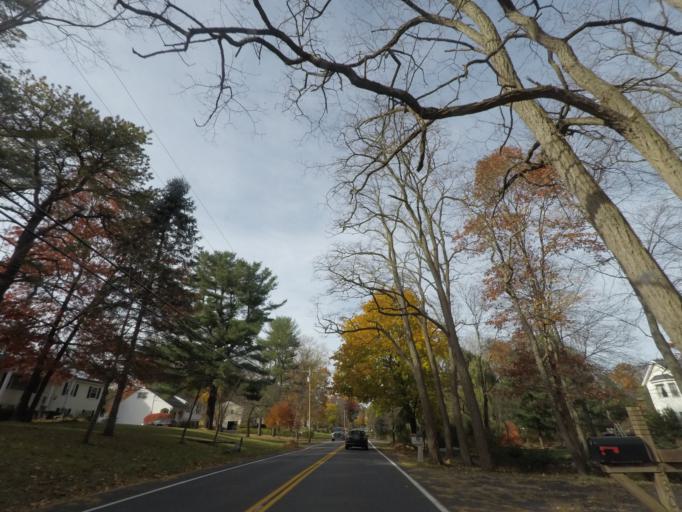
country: US
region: New York
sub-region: Schenectady County
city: Rotterdam
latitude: 42.7420
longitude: -73.9221
